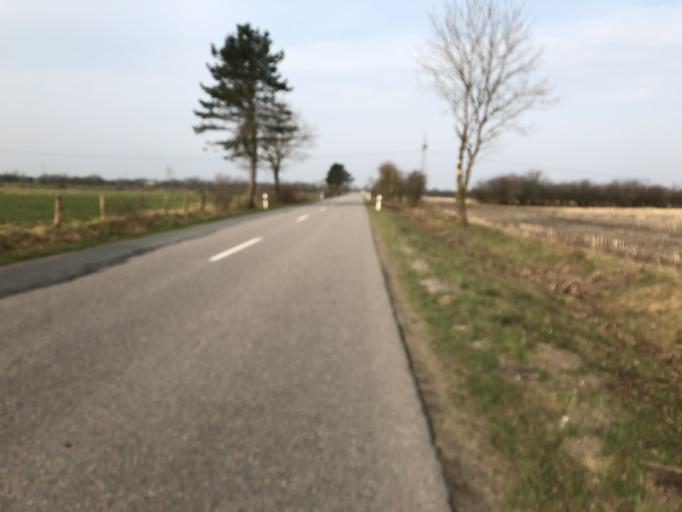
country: DE
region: Schleswig-Holstein
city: Sankelmark
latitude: 54.7044
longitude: 9.4199
